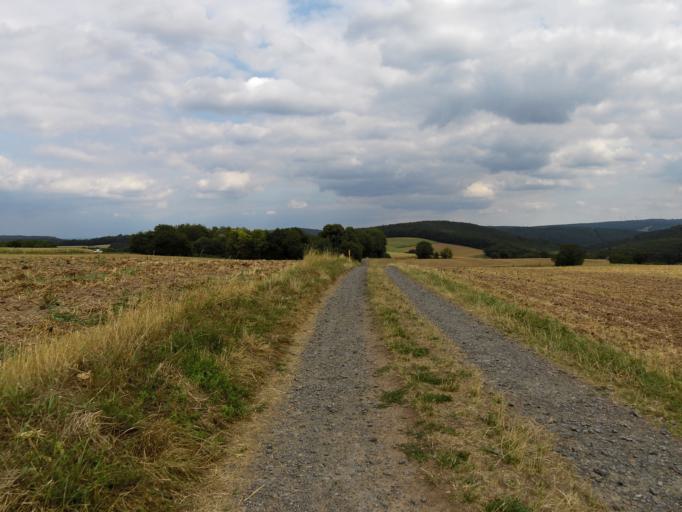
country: DE
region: Hesse
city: Hochst im Odenwald
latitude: 49.7736
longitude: 8.9470
